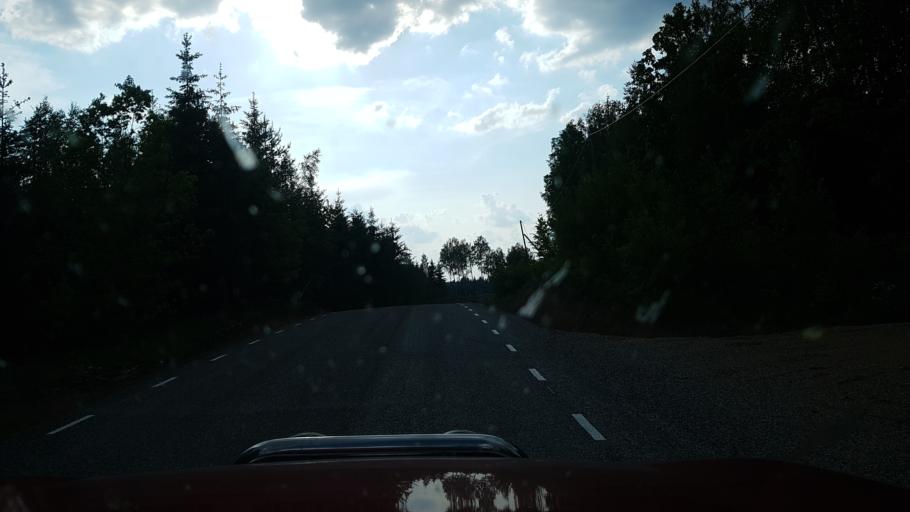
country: EE
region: Tartu
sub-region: UElenurme vald
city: Ulenurme
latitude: 58.1079
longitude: 26.7508
